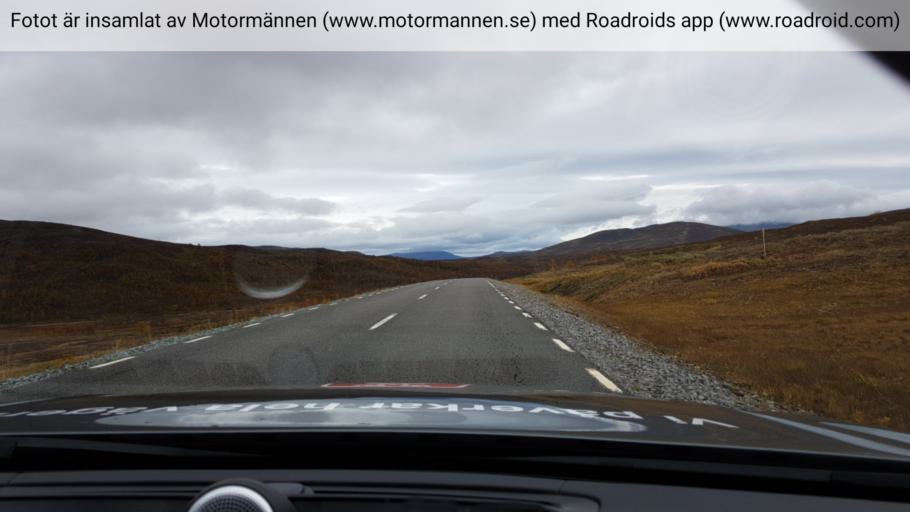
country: NO
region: Nordland
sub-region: Hattfjelldal
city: Hattfjelldal
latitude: 65.1141
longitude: 14.4944
